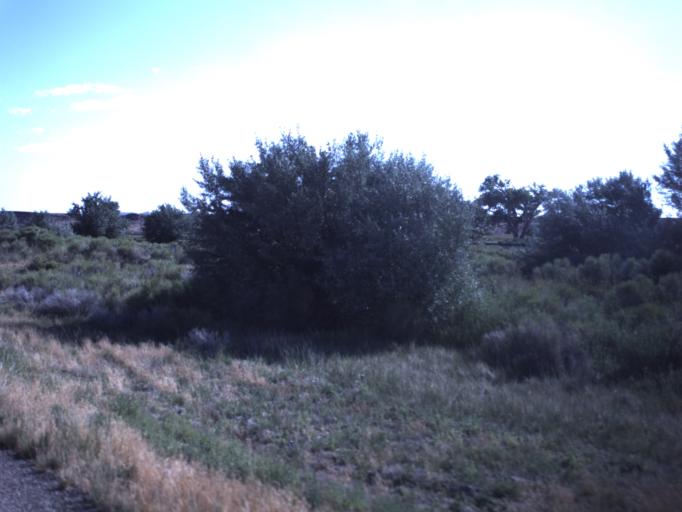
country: US
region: Utah
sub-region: Beaver County
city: Milford
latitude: 38.7153
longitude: -112.9690
